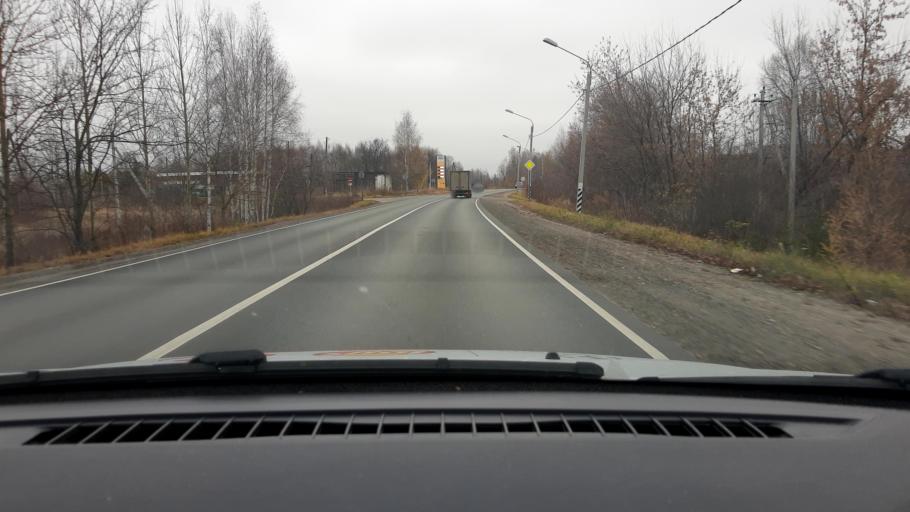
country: RU
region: Nizjnij Novgorod
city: Gorodets
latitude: 56.5997
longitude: 43.4534
